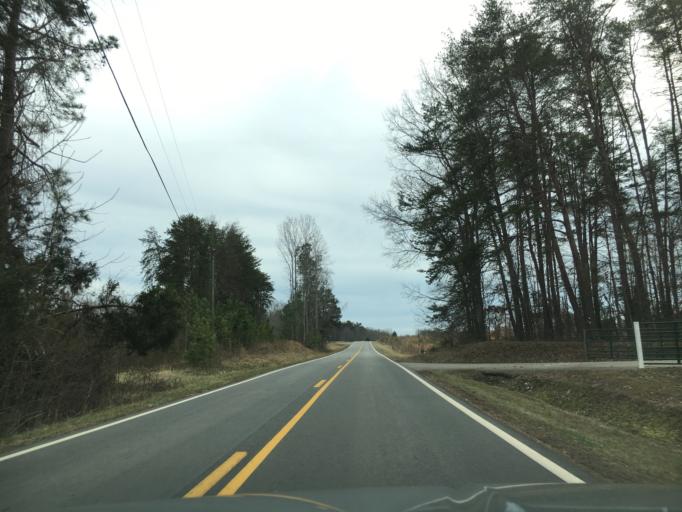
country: US
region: Virginia
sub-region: Charlotte County
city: Charlotte Court House
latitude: 37.0951
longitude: -78.7454
